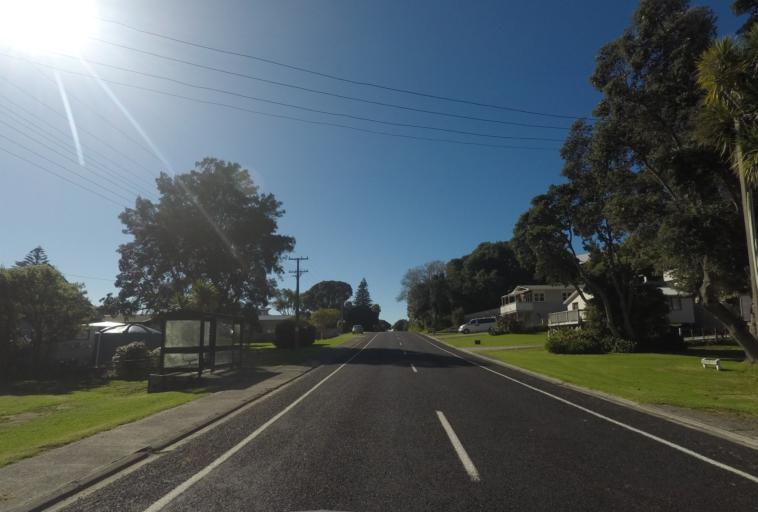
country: NZ
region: Waikato
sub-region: Thames-Coromandel District
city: Whangamata
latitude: -37.2838
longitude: 175.8980
